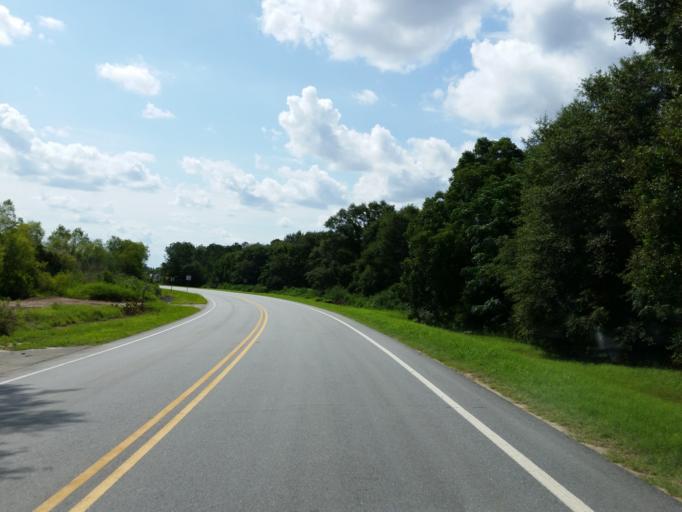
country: US
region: Georgia
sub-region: Turner County
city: Ashburn
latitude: 31.6646
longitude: -83.6034
